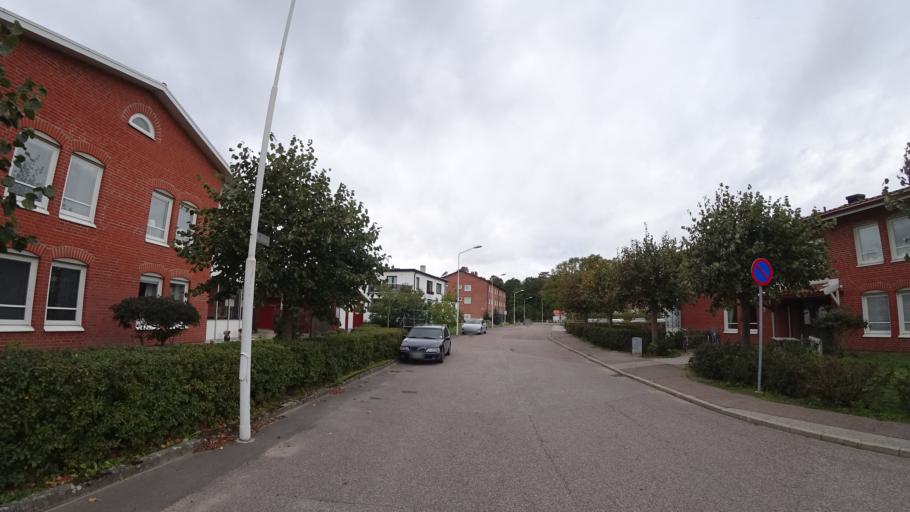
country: SE
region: Skane
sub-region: Kavlinge Kommun
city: Kaevlinge
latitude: 55.7748
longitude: 13.0959
